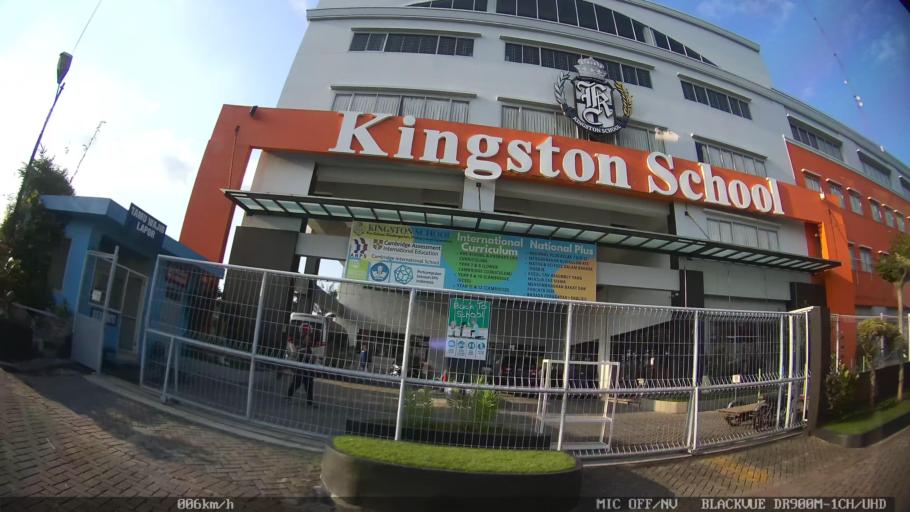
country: ID
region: North Sumatra
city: Medan
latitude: 3.6204
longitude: 98.6550
